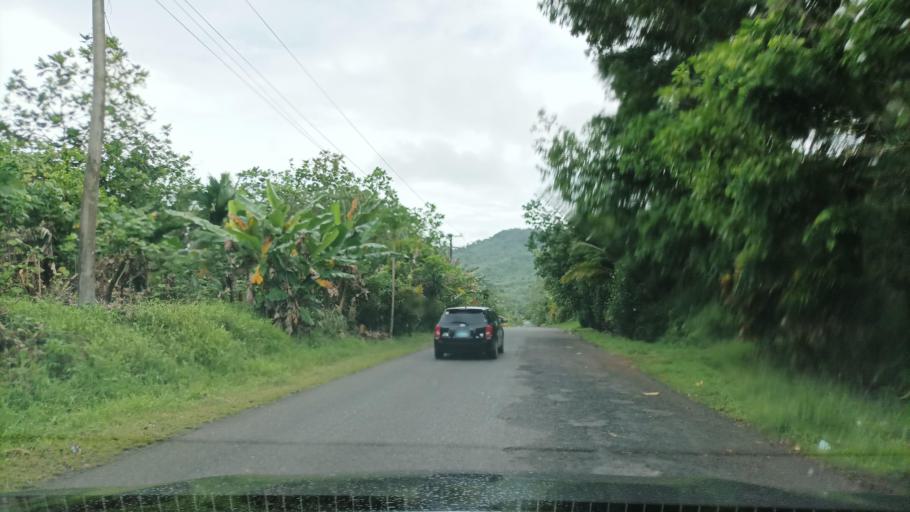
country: FM
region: Pohnpei
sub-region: Madolenihm Municipality
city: Madolenihm Municipality Government
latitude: 6.9218
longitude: 158.2875
